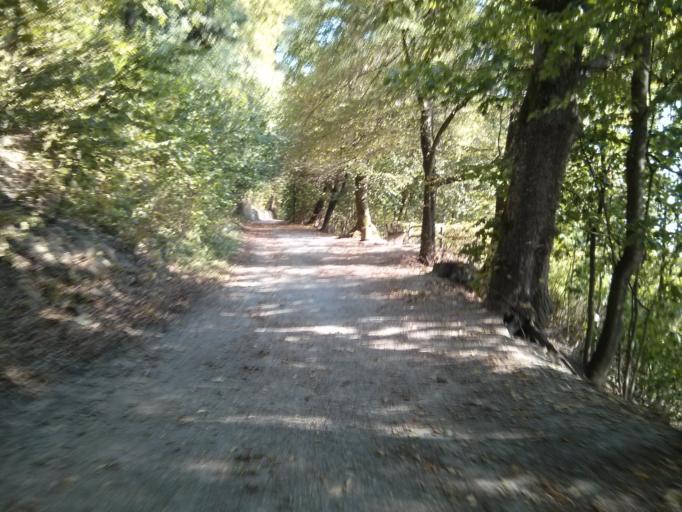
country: DE
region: Bavaria
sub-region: Lower Bavaria
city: Deggendorf
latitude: 48.8278
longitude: 12.9646
